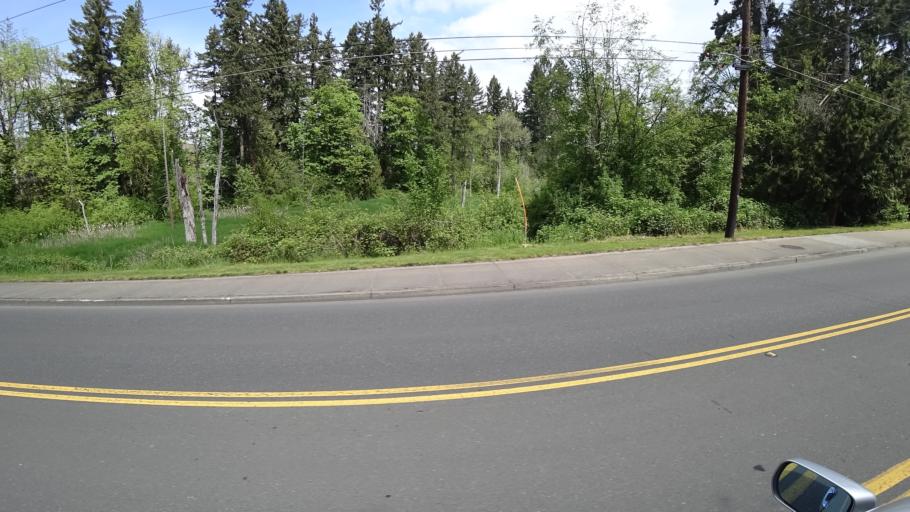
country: US
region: Oregon
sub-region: Washington County
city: Hillsboro
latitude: 45.5358
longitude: -122.9925
